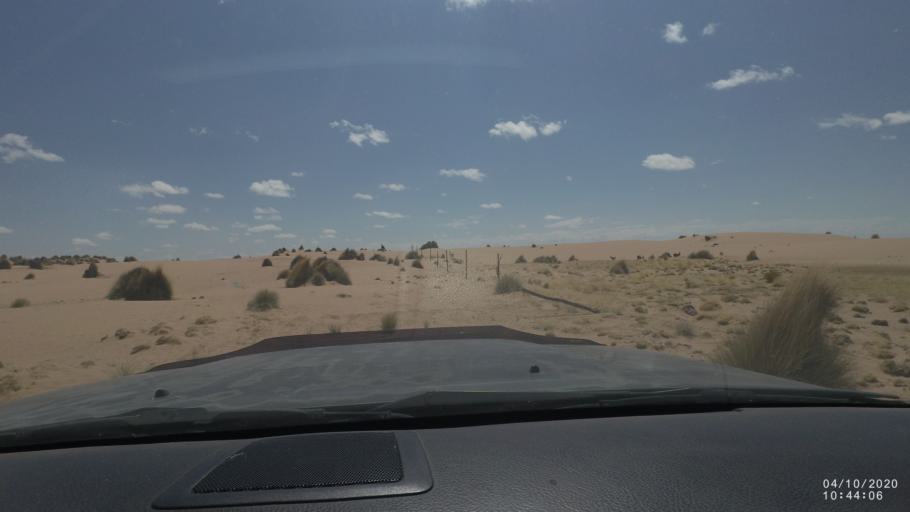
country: BO
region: Oruro
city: Poopo
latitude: -18.7041
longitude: -67.4709
